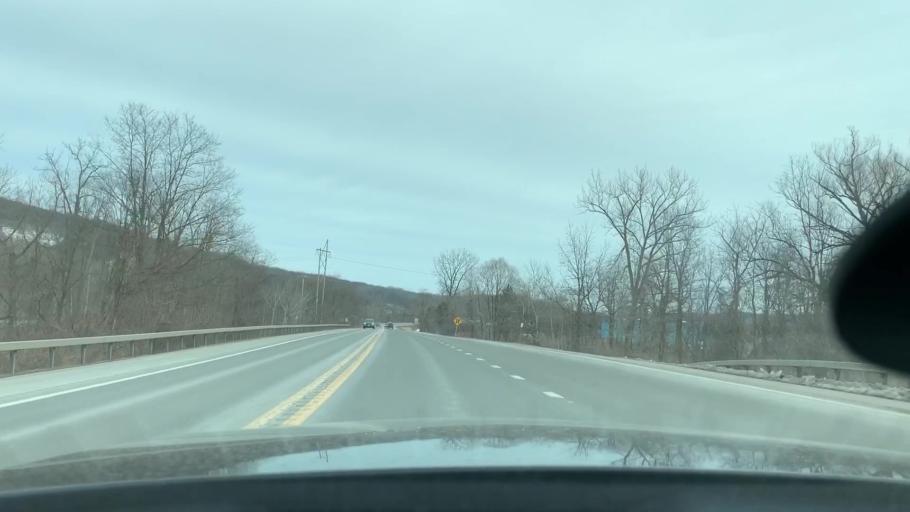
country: US
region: New York
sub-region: Herkimer County
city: Ilion
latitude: 43.0219
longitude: -75.0429
